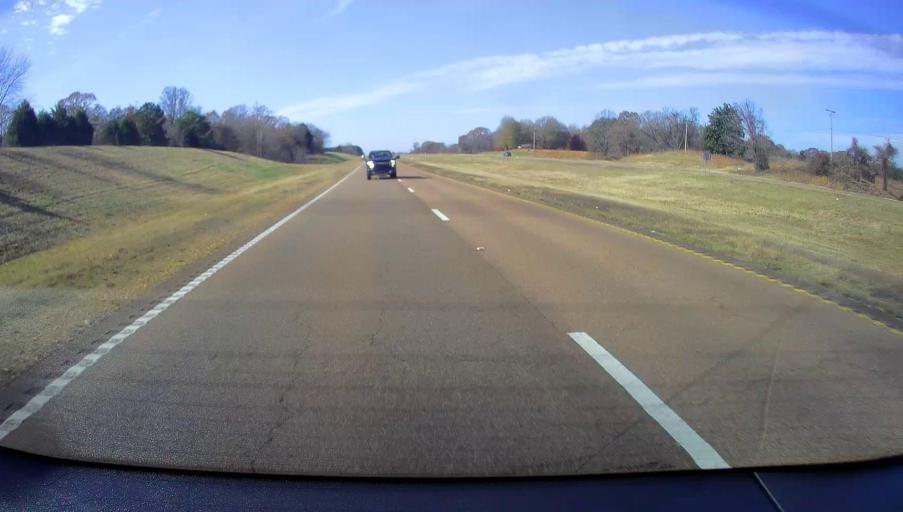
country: US
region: Mississippi
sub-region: Marshall County
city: Holly Springs
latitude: 34.9461
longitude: -89.3570
